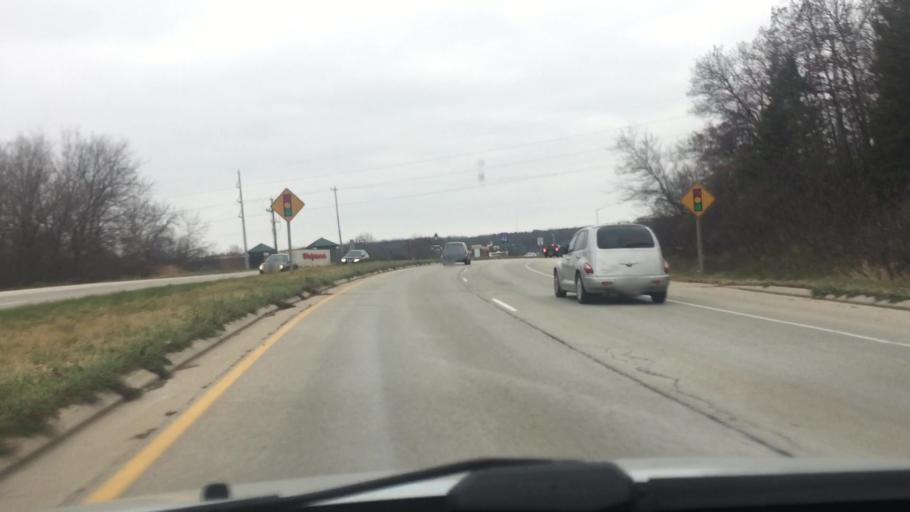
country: US
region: Wisconsin
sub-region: Waukesha County
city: Delafield
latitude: 43.0564
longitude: -88.3694
